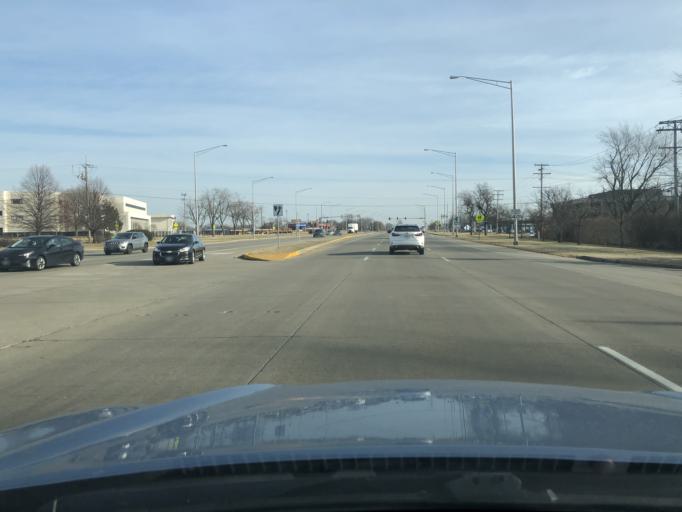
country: US
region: Illinois
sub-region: Cook County
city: Hoffman Estates
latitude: 42.0522
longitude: -88.1106
